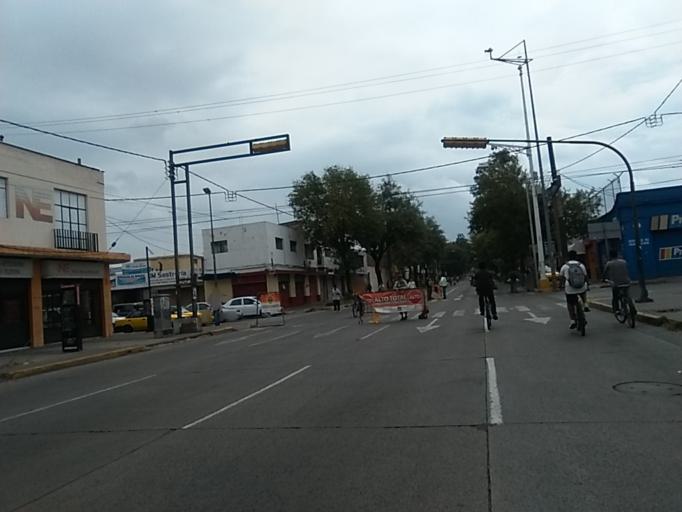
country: MX
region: Jalisco
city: Tlaquepaque
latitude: 20.6726
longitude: -103.3308
